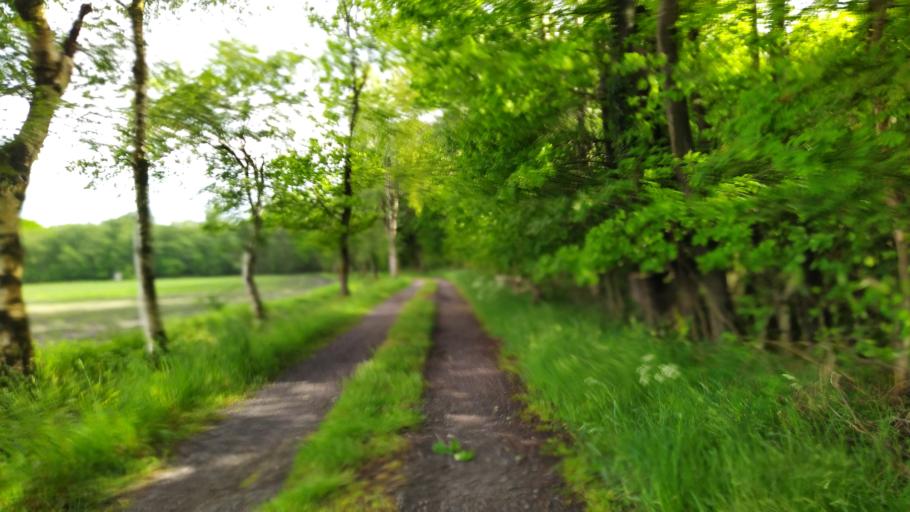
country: DE
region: Lower Saxony
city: Brest
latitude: 53.4262
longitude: 9.3555
